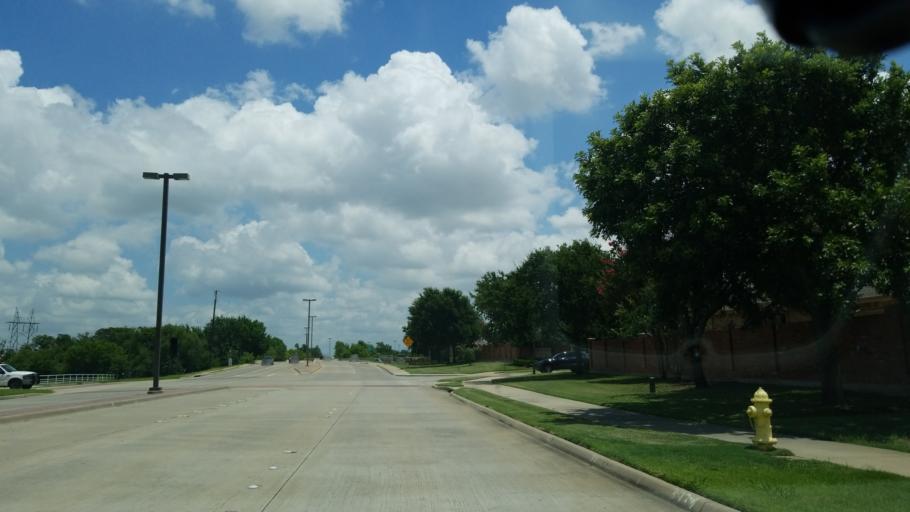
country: US
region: Texas
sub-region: Dallas County
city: Carrollton
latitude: 32.9659
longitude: -96.9467
